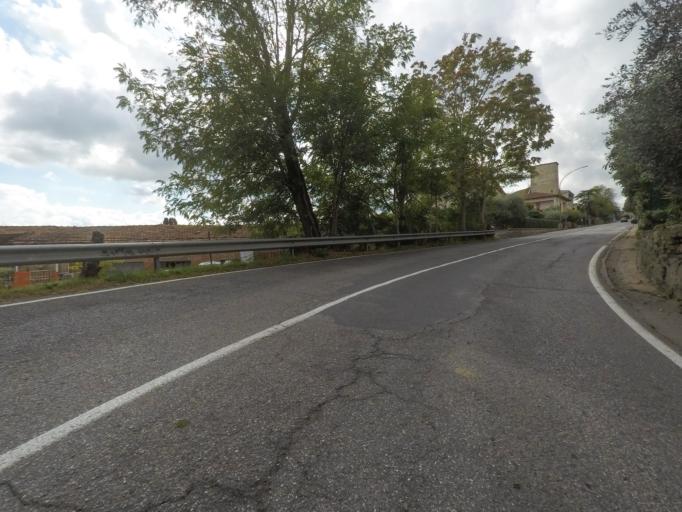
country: IT
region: Tuscany
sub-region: Provincia di Siena
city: Torrita di Siena
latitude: 43.1684
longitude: 11.7751
